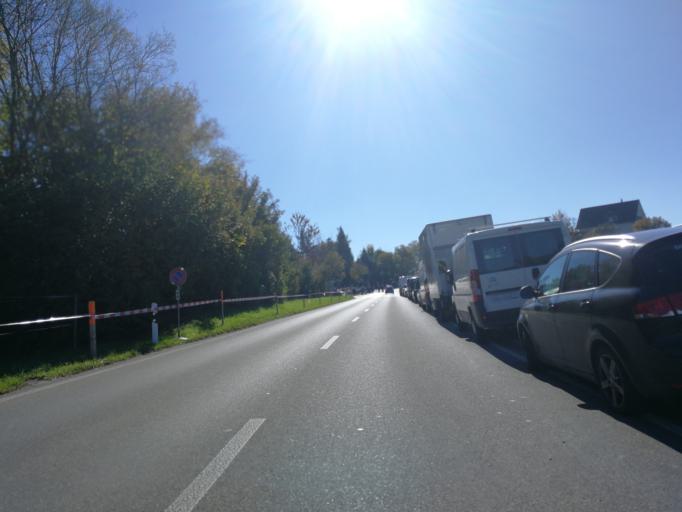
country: CH
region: Zurich
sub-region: Bezirk Hinwil
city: Binzikon
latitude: 47.2848
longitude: 8.7665
